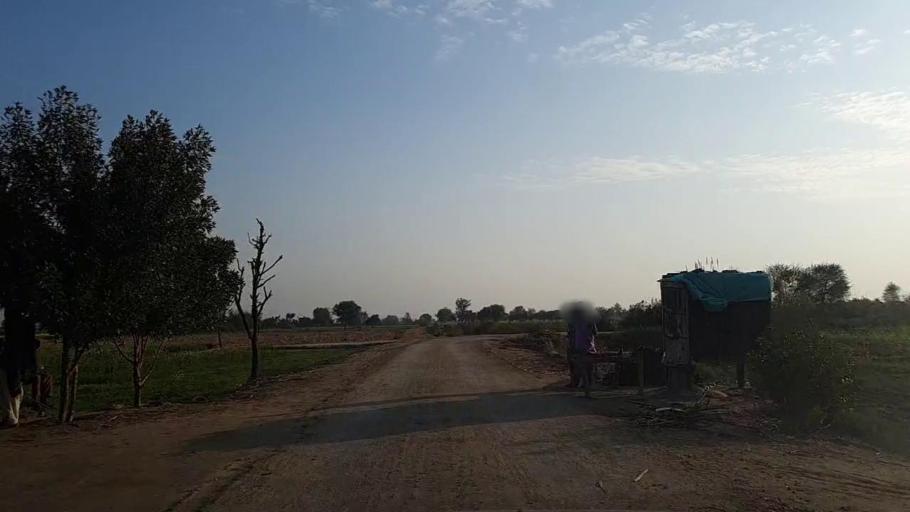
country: PK
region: Sindh
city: Jam Sahib
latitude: 26.3950
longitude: 68.5238
